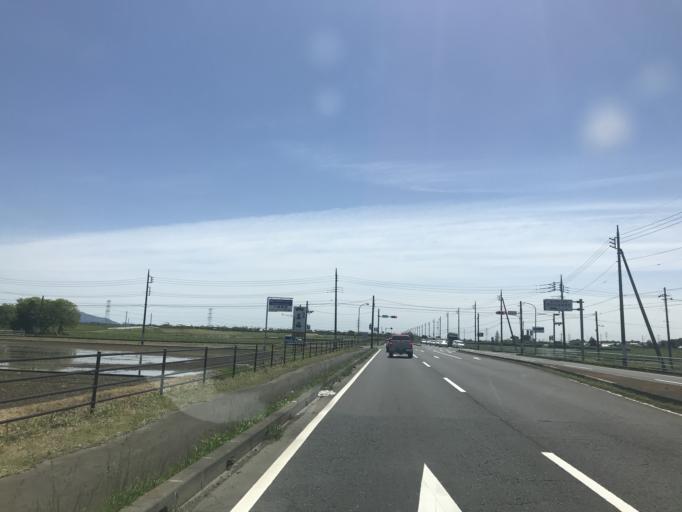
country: JP
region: Ibaraki
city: Shimodate
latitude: 36.2733
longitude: 139.9797
